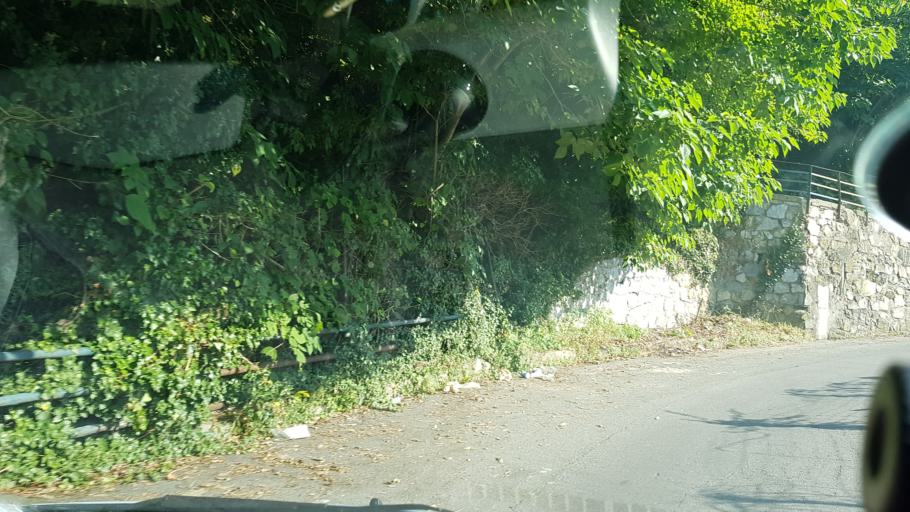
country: IT
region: Liguria
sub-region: Provincia di Genova
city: Genoa
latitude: 44.4421
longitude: 8.8967
